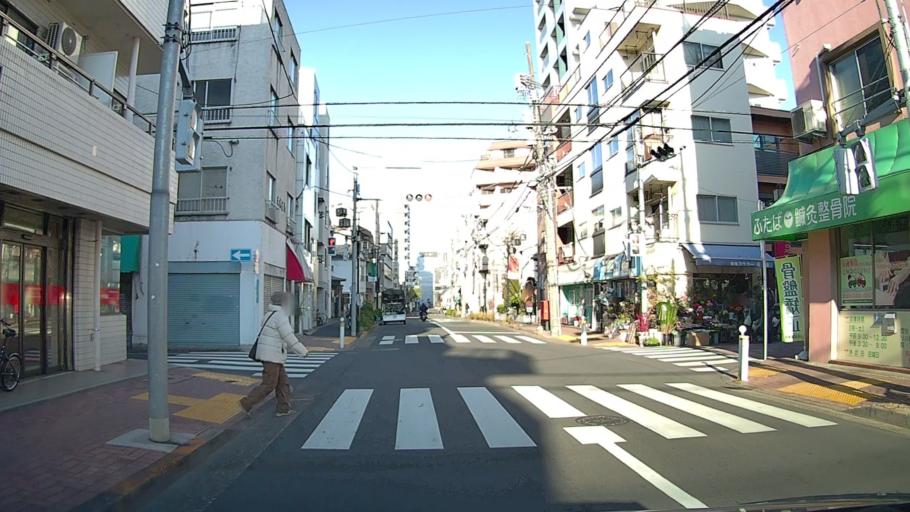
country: JP
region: Tokyo
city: Tokyo
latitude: 35.6878
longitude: 139.6725
